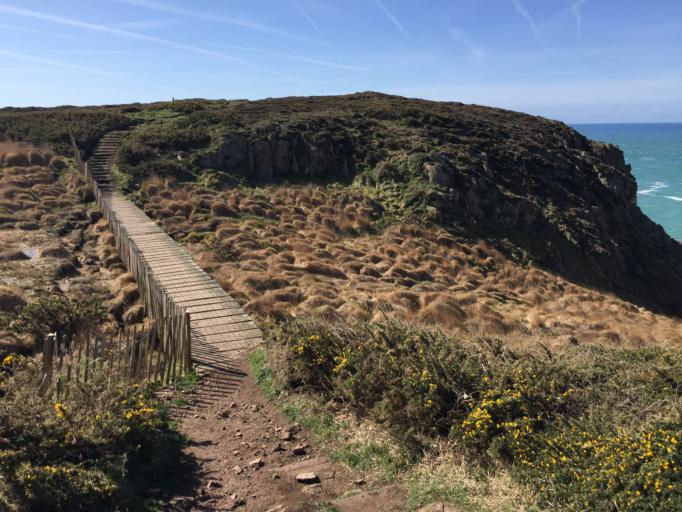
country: JE
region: St Helier
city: Saint Helier
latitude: 49.2490
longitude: -2.2510
